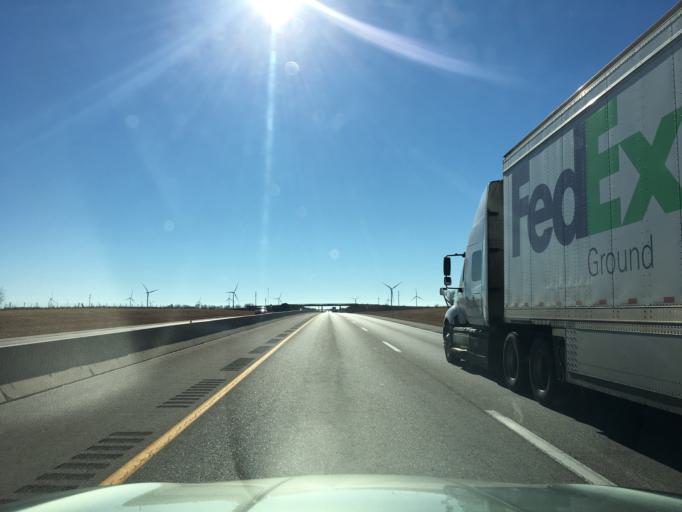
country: US
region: Kansas
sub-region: Sumner County
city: Wellington
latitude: 37.1639
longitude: -97.3395
